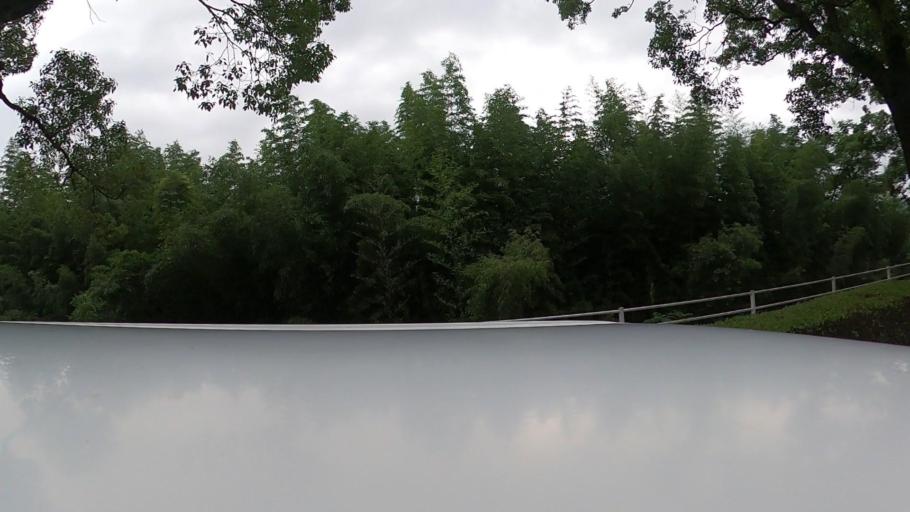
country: JP
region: Kumamoto
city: Ozu
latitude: 32.8315
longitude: 130.8568
